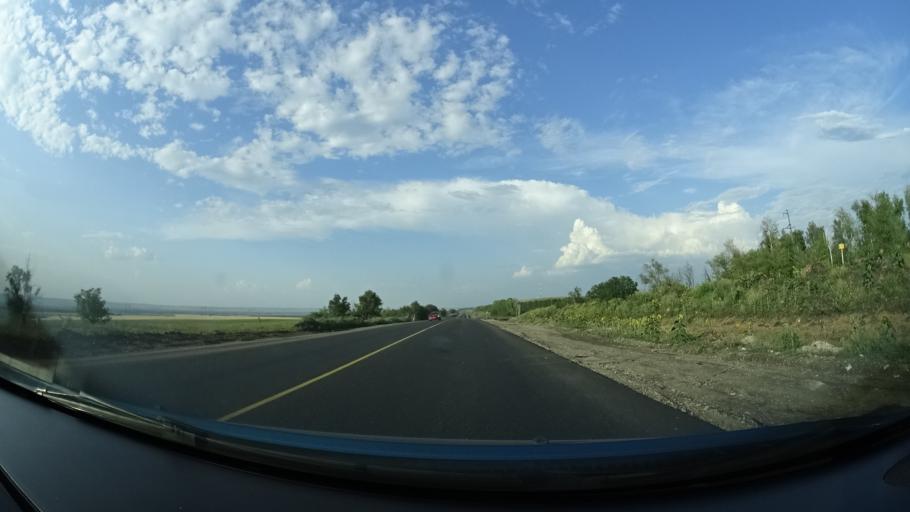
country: RU
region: Samara
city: Sukhodol
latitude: 53.7468
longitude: 50.8625
